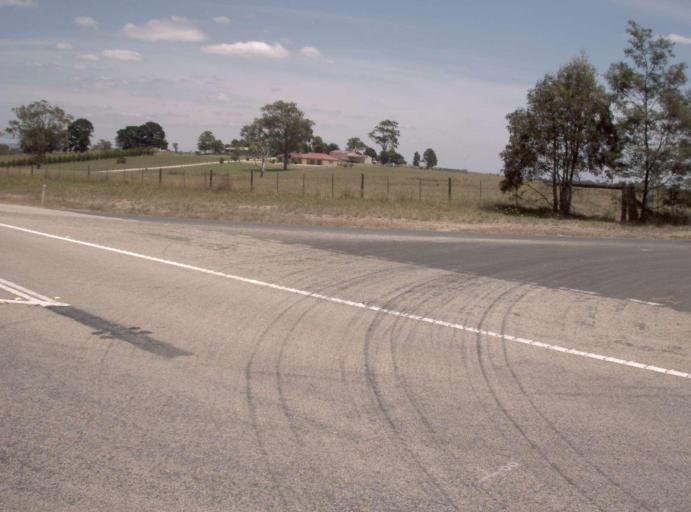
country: AU
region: Victoria
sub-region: East Gippsland
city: Bairnsdale
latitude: -37.7790
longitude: 147.6842
